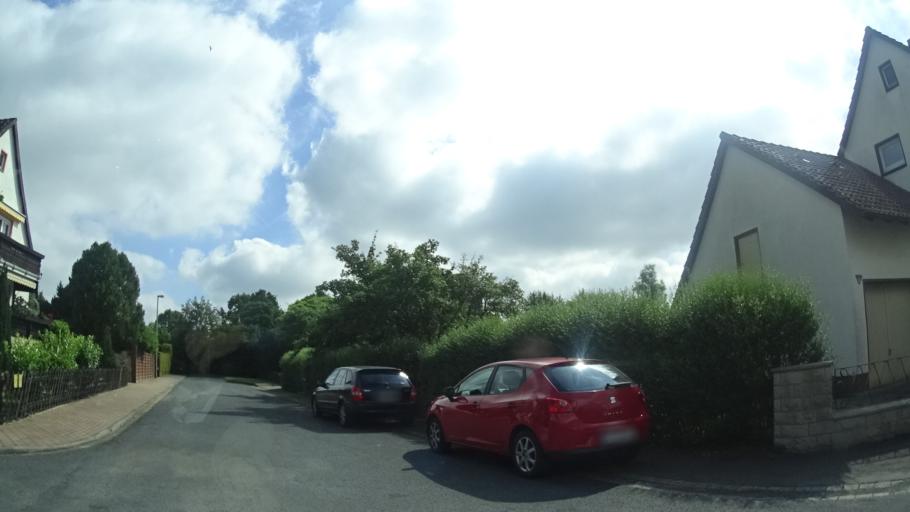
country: DE
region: Lower Saxony
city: Harsum
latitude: 52.1977
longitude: 9.9718
